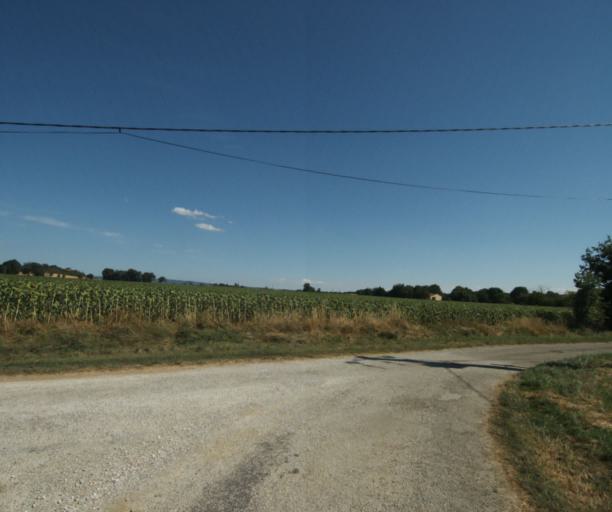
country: FR
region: Midi-Pyrenees
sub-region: Departement de la Haute-Garonne
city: Saint-Felix-Lauragais
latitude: 43.5001
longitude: 1.9087
